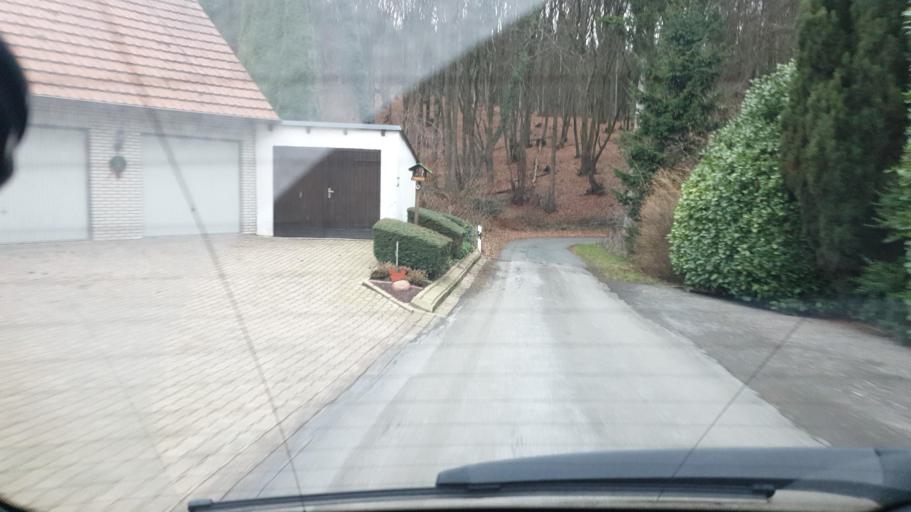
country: DE
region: North Rhine-Westphalia
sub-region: Regierungsbezirk Detmold
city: Hille
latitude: 52.2793
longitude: 8.7544
